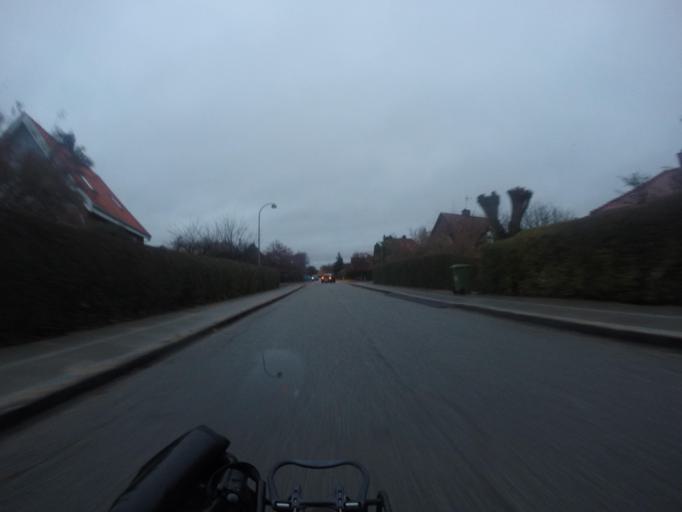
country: DK
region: Capital Region
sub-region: Gladsaxe Municipality
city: Buddinge
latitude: 55.7514
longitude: 12.4596
